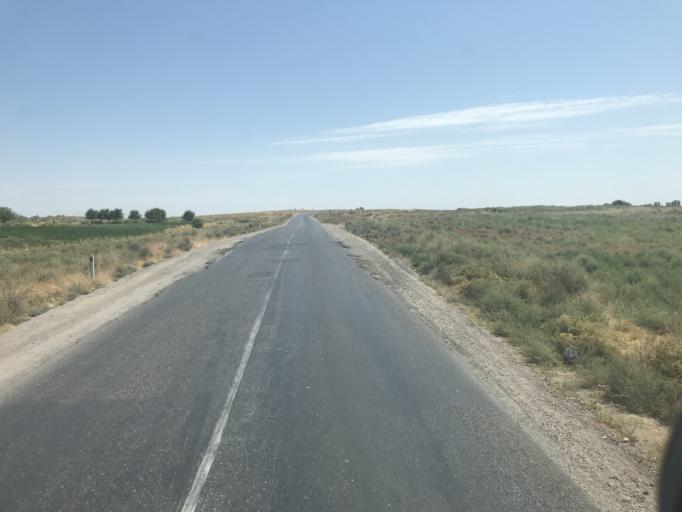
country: UZ
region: Toshkent
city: Yangiyul
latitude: 41.3475
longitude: 68.8722
